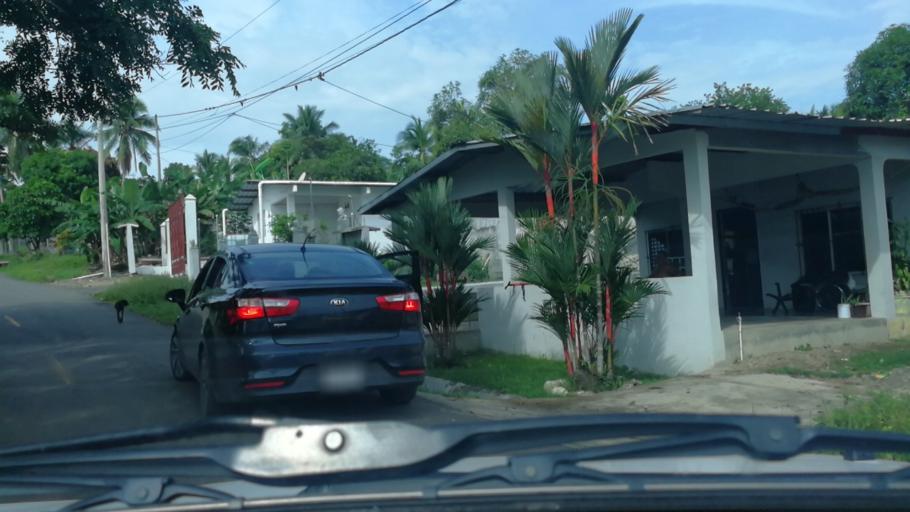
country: PA
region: Panama
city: Pacora
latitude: 9.0844
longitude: -79.2942
